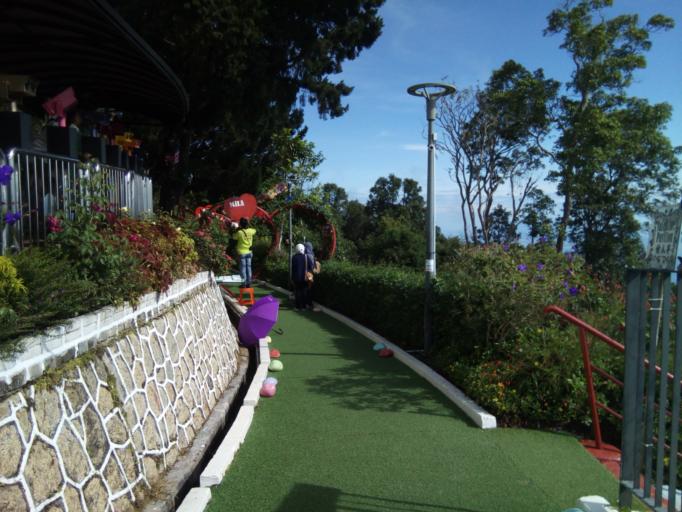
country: MY
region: Penang
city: Tanjung Tokong
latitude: 5.4241
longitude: 100.2700
